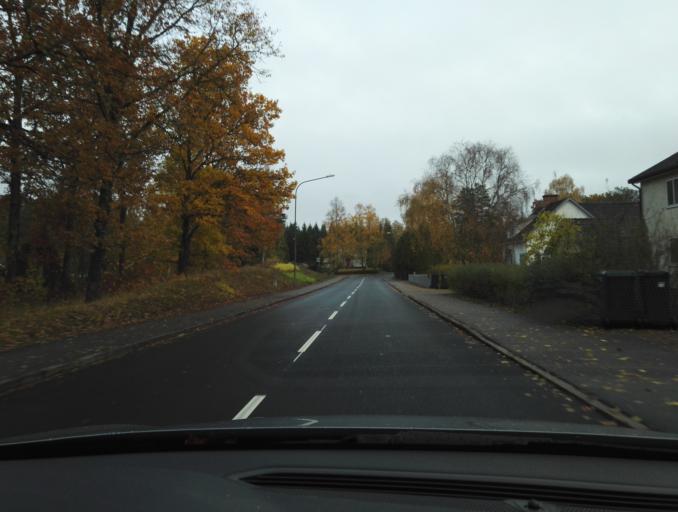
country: SE
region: Kronoberg
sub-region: Vaxjo Kommun
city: Rottne
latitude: 57.0298
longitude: 14.7791
